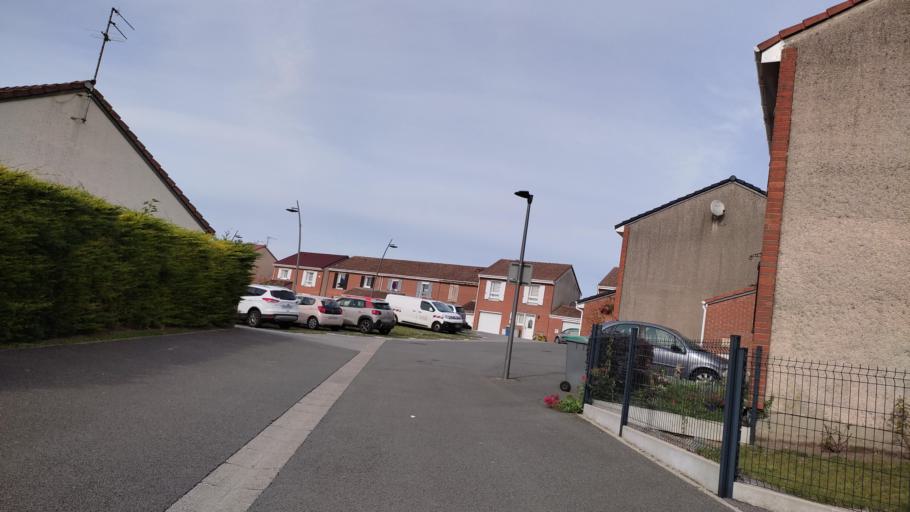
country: FR
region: Nord-Pas-de-Calais
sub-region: Departement du Pas-de-Calais
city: Feuchy
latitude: 50.3053
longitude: 2.8374
